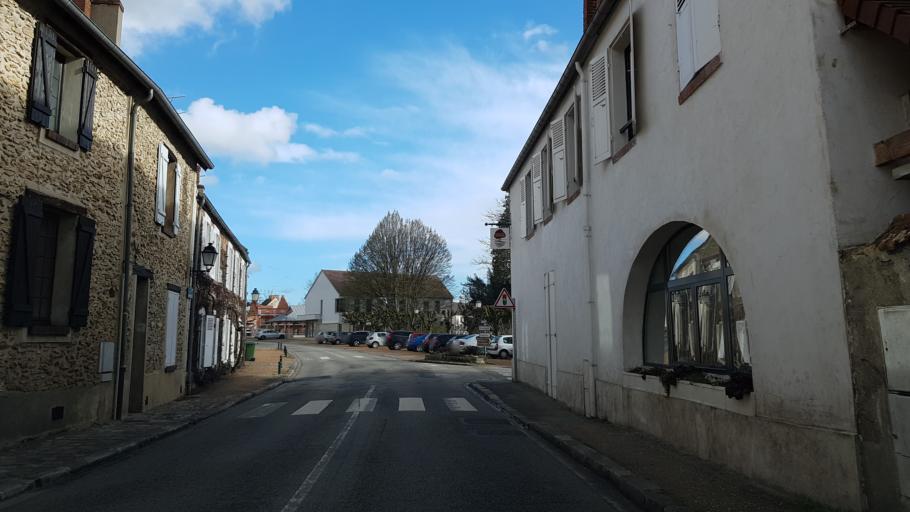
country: FR
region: Ile-de-France
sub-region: Departement des Yvelines
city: Sonchamp
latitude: 48.6133
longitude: 1.9075
